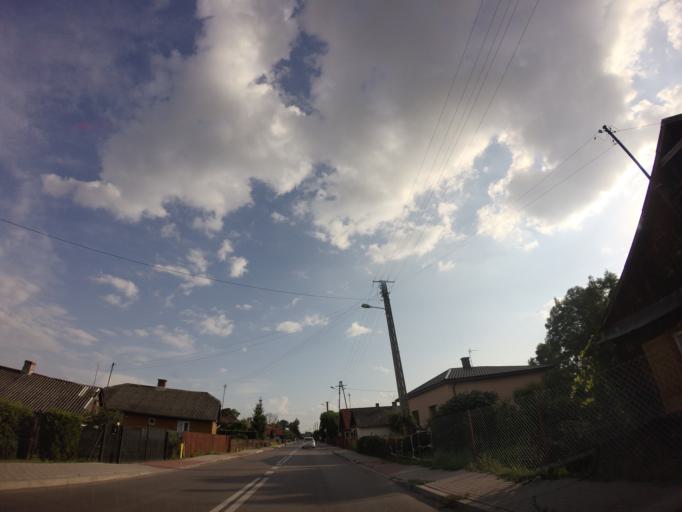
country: PL
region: Lublin Voivodeship
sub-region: Powiat lubartowski
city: Jeziorzany
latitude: 51.6059
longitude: 22.2785
